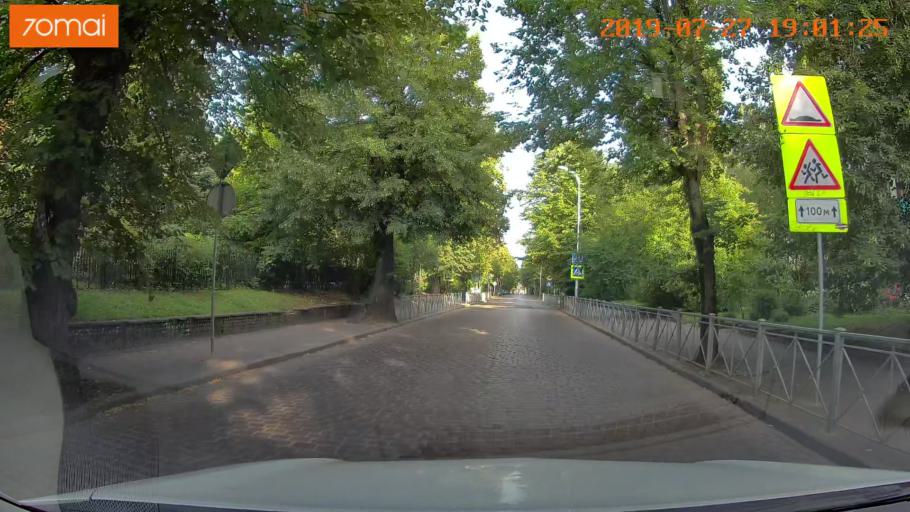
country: RU
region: Kaliningrad
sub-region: Gorod Kaliningrad
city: Kaliningrad
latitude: 54.7265
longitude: 20.4883
